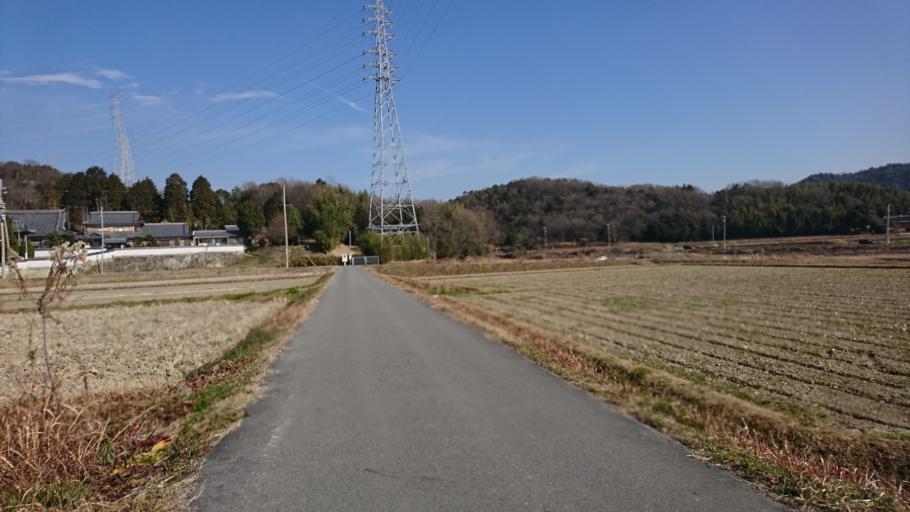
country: JP
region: Hyogo
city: Kakogawacho-honmachi
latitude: 34.8074
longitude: 134.8634
